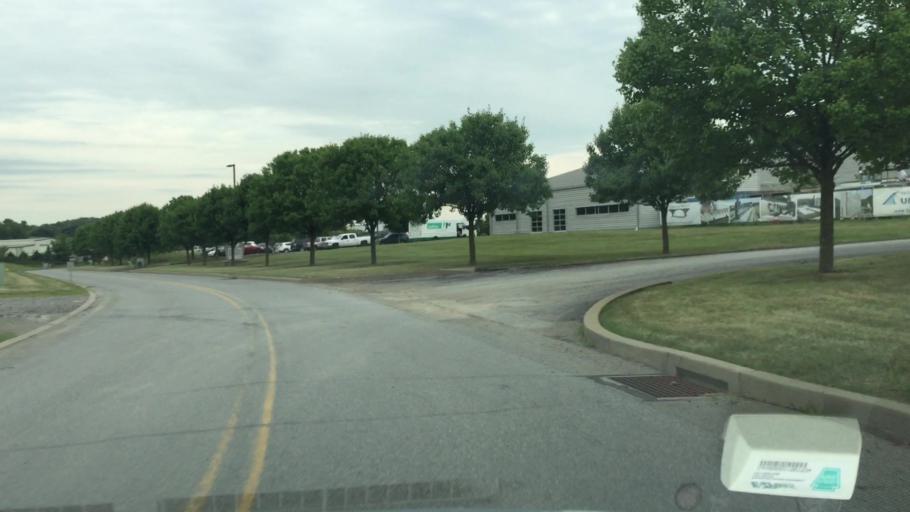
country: US
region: Pennsylvania
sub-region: Butler County
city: Saxonburg
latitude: 40.7308
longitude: -79.8458
